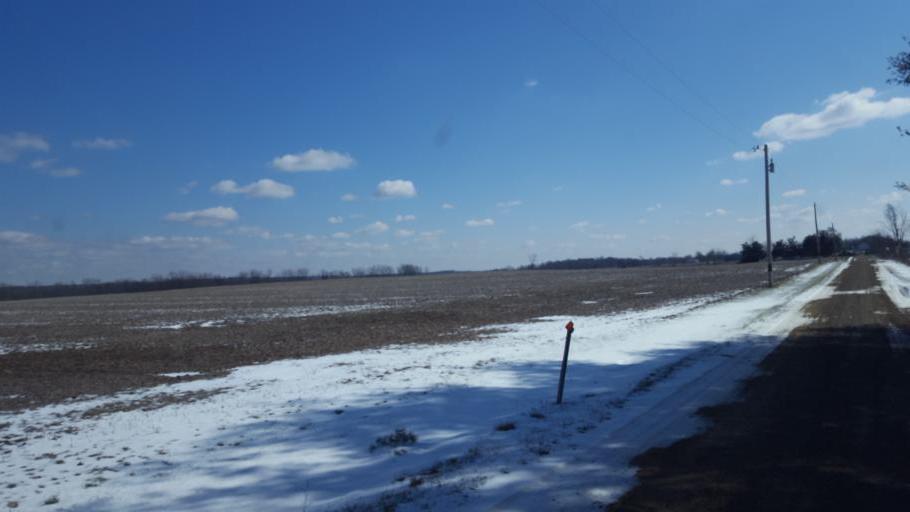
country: US
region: Ohio
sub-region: Licking County
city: Utica
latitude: 40.2885
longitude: -82.4896
